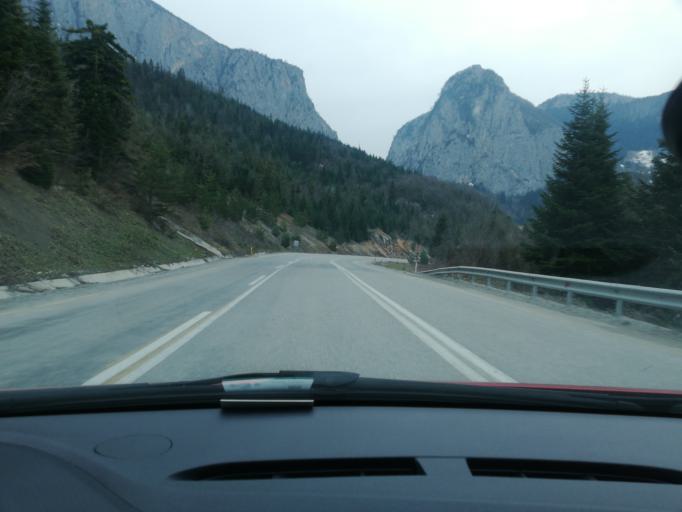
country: TR
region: Kastamonu
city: Kure
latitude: 41.8455
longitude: 33.7237
